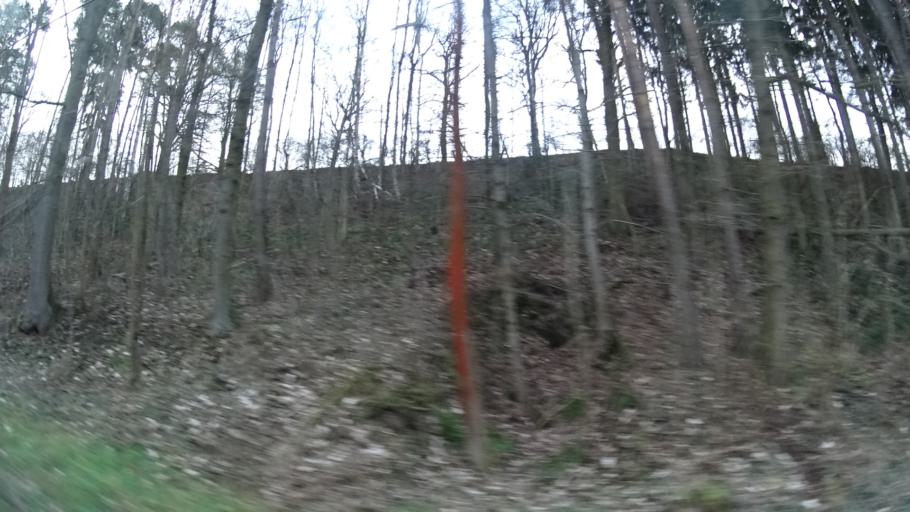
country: DE
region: Thuringia
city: Bibra
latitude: 50.8095
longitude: 11.5474
